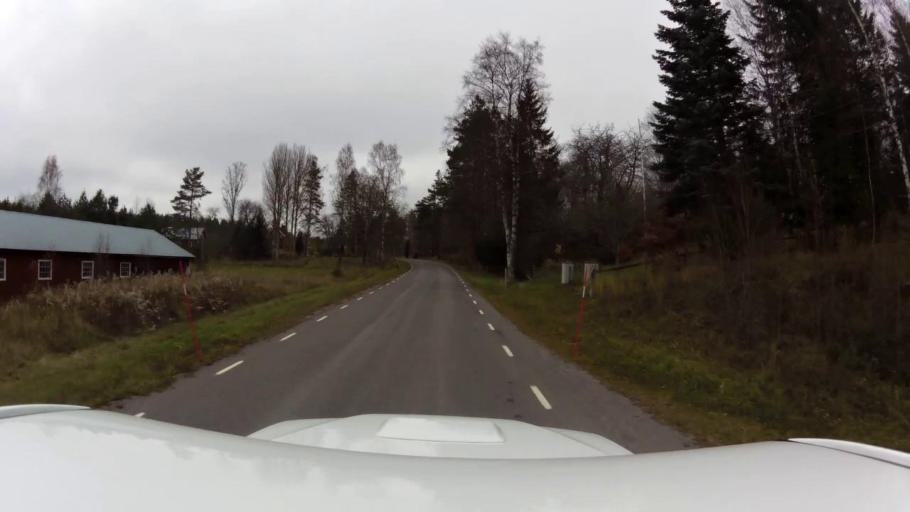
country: SE
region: OEstergoetland
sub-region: Kinda Kommun
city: Kisa
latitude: 58.1311
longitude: 15.4534
